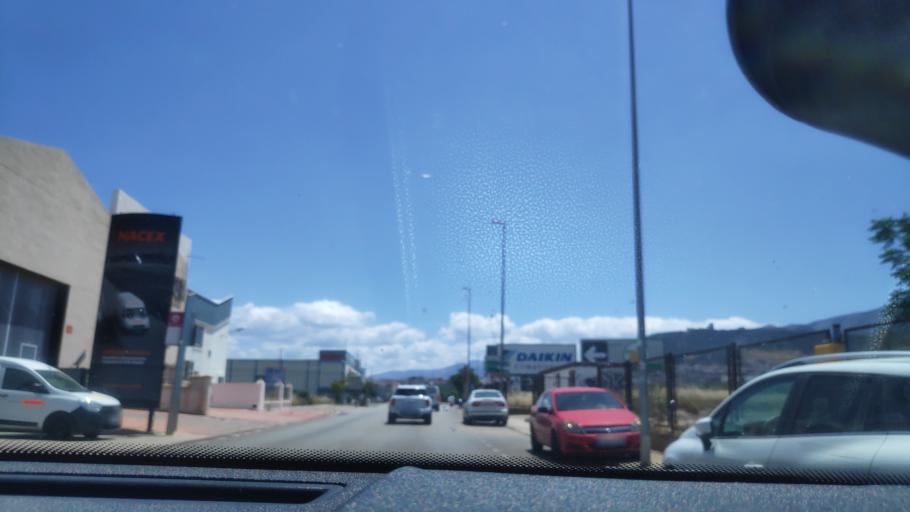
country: ES
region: Andalusia
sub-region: Provincia de Jaen
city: Jaen
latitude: 37.7953
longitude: -3.7927
